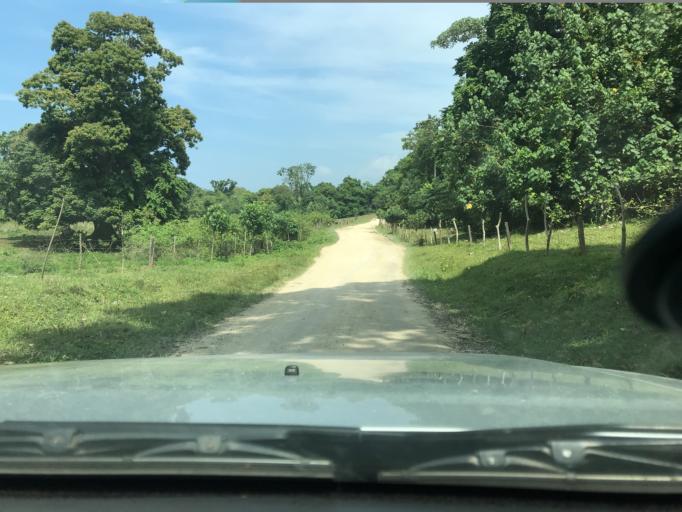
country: VU
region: Sanma
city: Luganville
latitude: -15.5805
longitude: 167.0131
